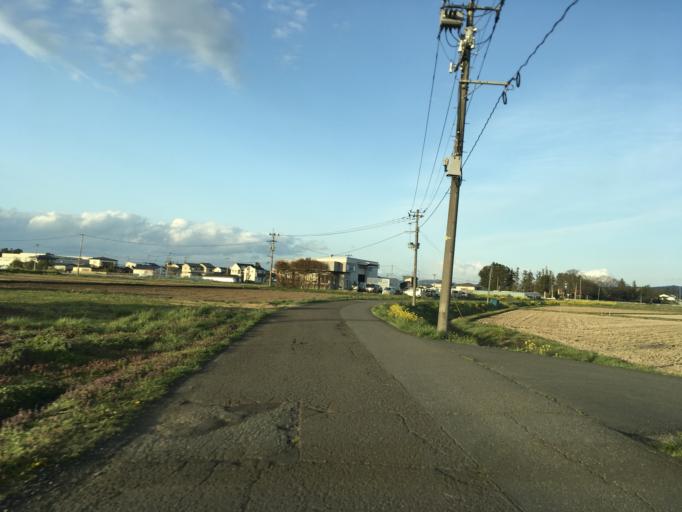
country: JP
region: Miyagi
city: Wakuya
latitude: 38.6663
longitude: 141.1903
